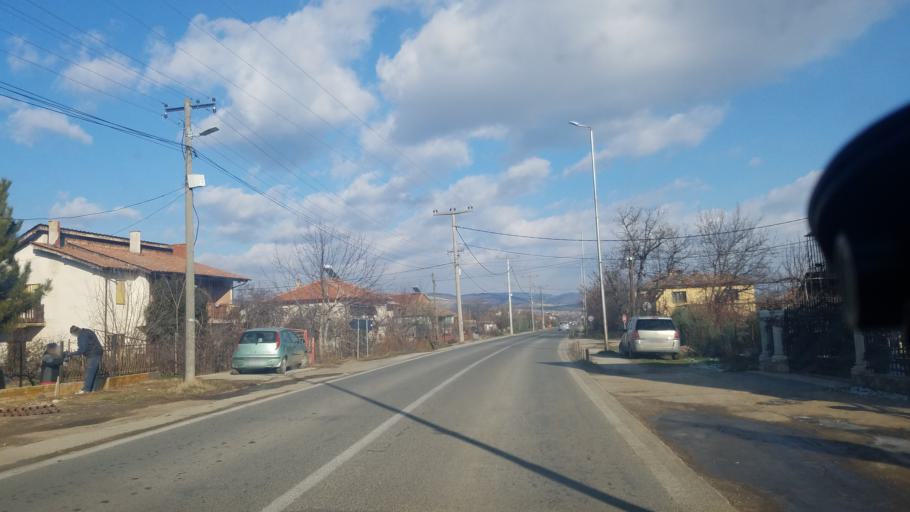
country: MK
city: Obleshevo
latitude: 41.8841
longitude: 22.3355
